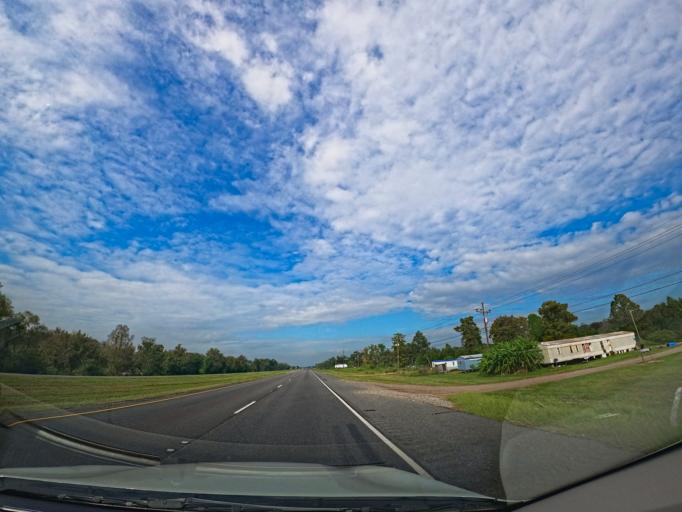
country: US
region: Louisiana
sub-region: Saint Mary Parish
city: Patterson
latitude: 29.6935
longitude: -91.3345
